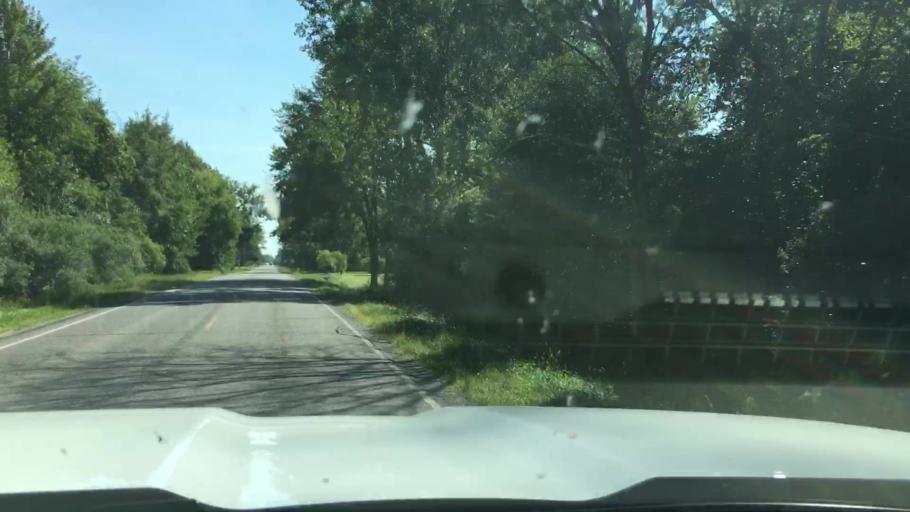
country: US
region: Michigan
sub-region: Saginaw County
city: Freeland
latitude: 43.5251
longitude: -84.1481
